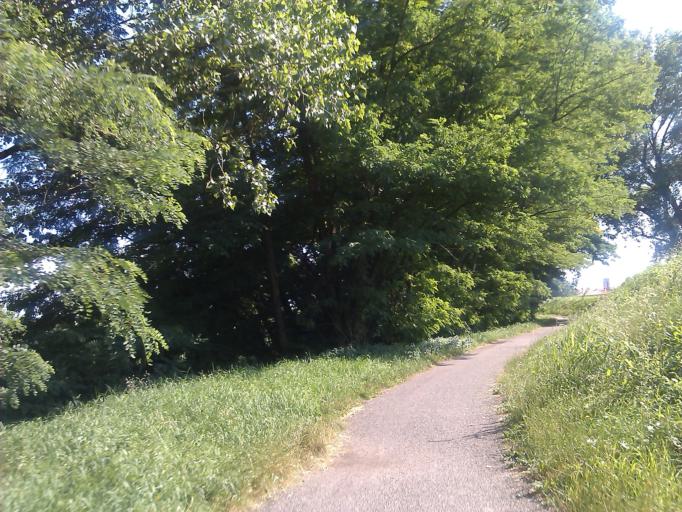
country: IT
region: Tuscany
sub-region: Province of Florence
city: Campi Bisenzio
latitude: 43.8591
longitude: 11.1250
